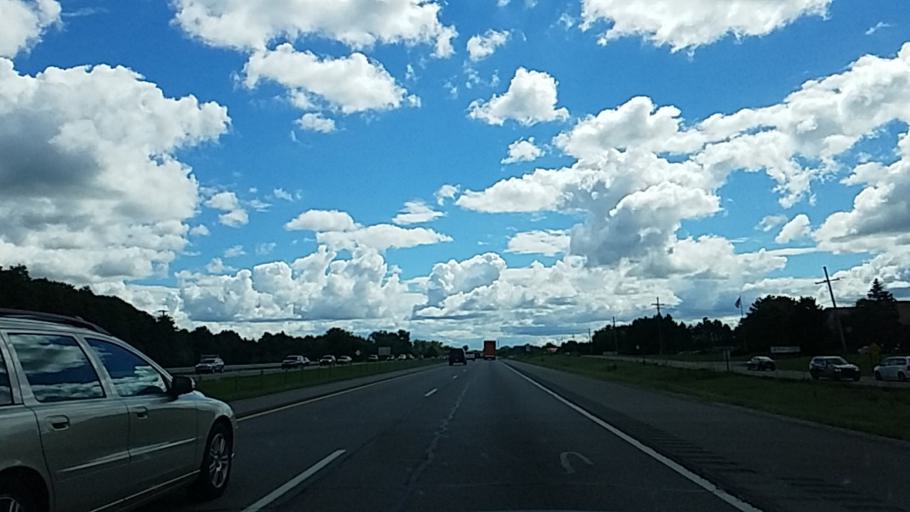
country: US
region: Michigan
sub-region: Livingston County
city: Brighton
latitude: 42.4988
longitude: -83.7579
